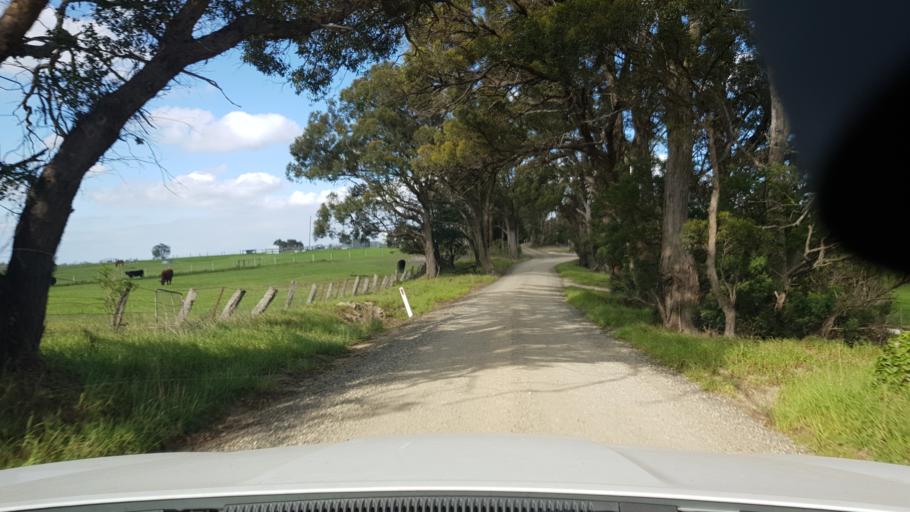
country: AU
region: Victoria
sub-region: East Gippsland
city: Bairnsdale
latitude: -37.7831
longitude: 147.5759
